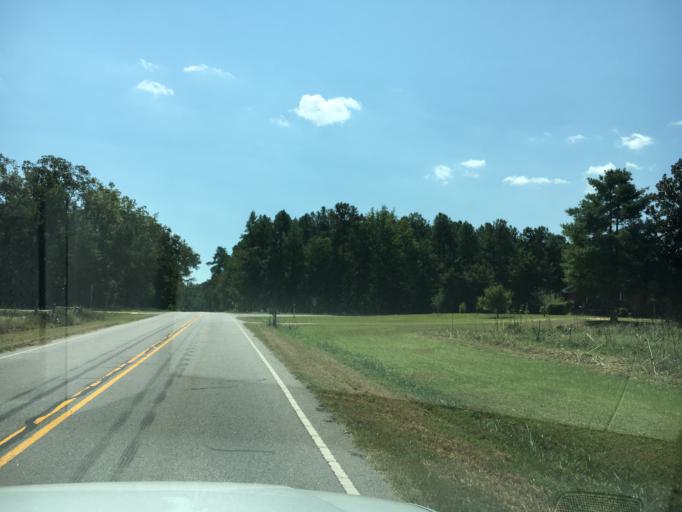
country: US
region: South Carolina
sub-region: Edgefield County
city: Johnston
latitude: 33.8778
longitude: -81.6950
